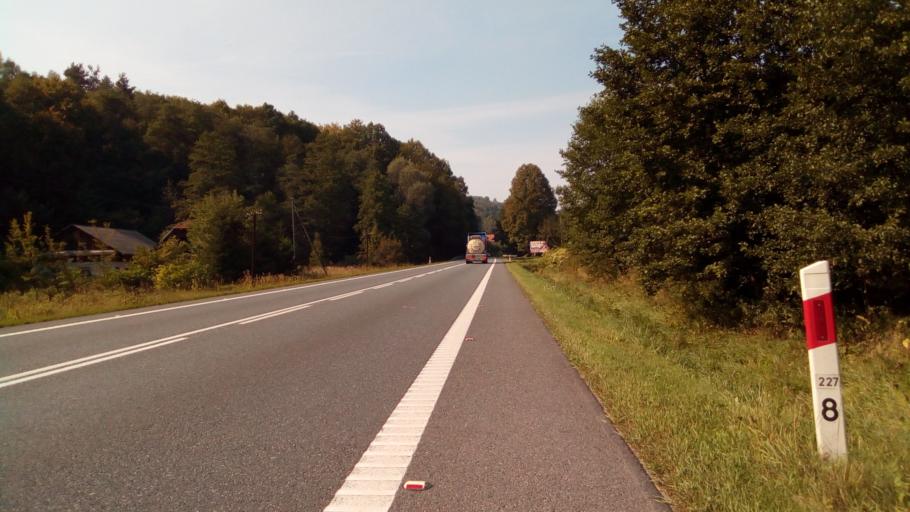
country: PL
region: Subcarpathian Voivodeship
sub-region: Powiat strzyzowski
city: Jawornik
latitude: 49.8130
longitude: 21.8809
